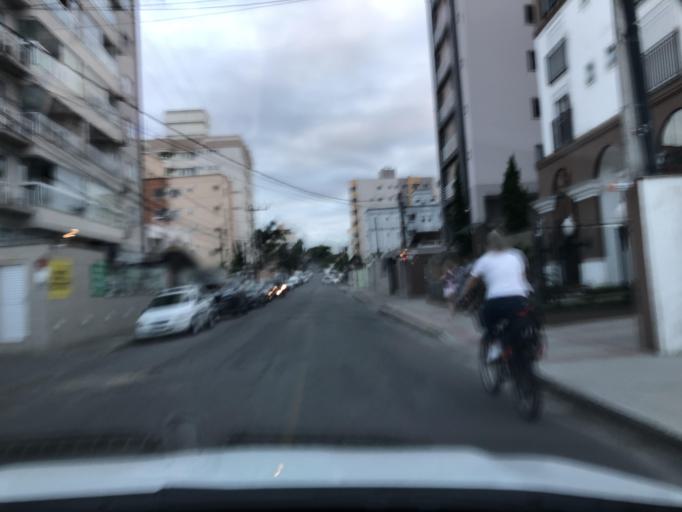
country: BR
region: Santa Catarina
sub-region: Joinville
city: Joinville
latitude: -26.2744
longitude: -48.8713
